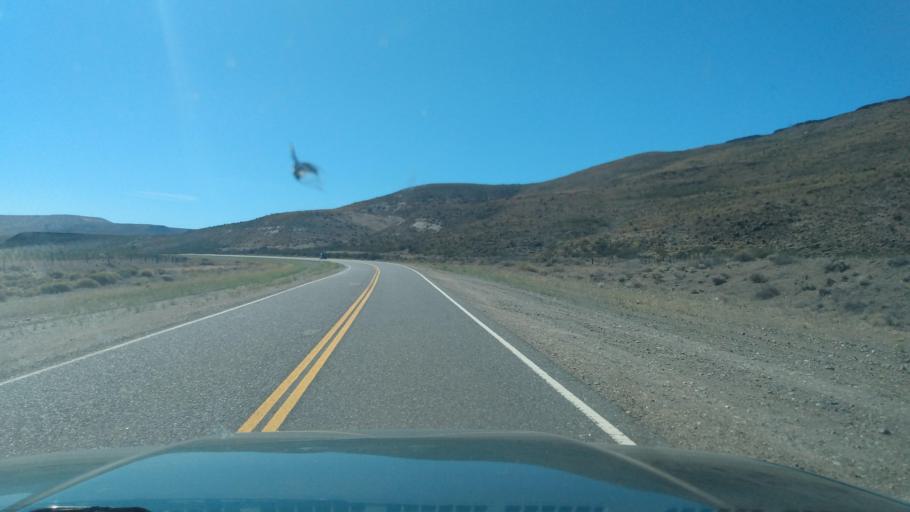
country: AR
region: Neuquen
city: Junin de los Andes
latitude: -40.0581
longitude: -70.7981
